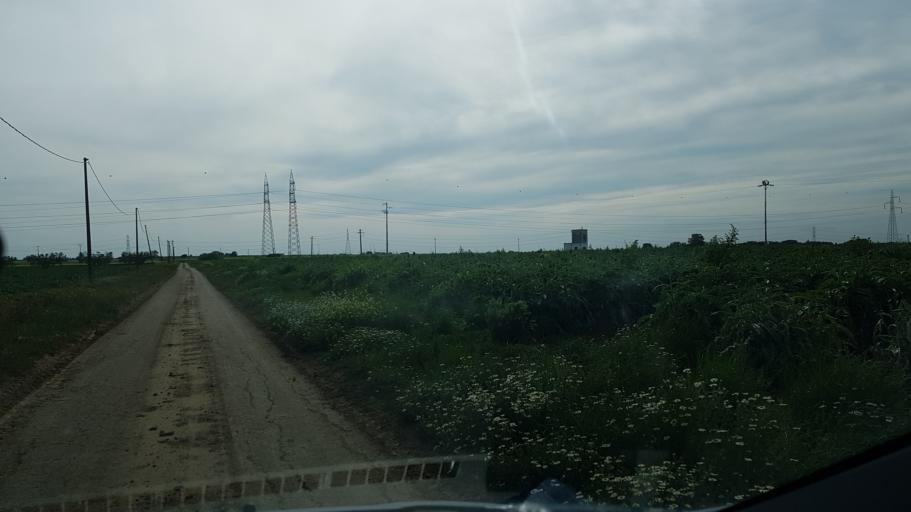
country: IT
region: Apulia
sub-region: Provincia di Brindisi
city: La Rosa
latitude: 40.5787
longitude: 17.9253
